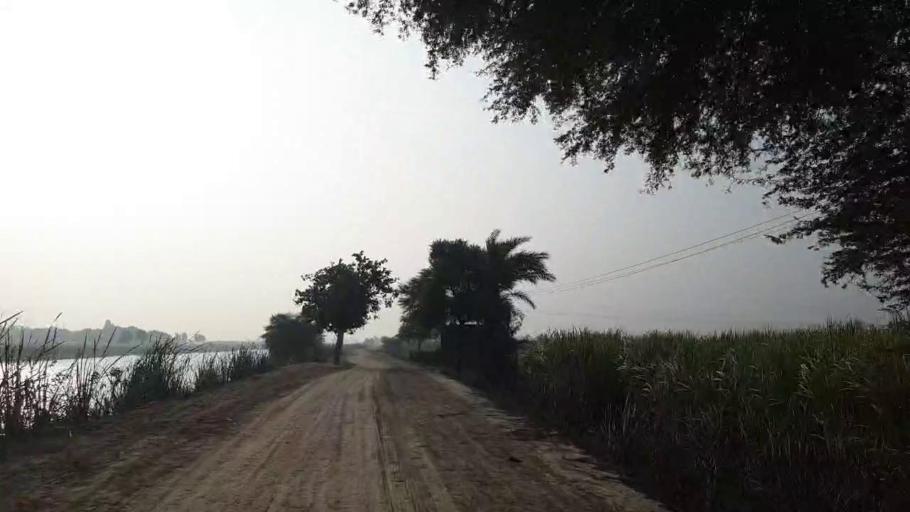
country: PK
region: Sindh
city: Tando Muhammad Khan
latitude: 25.1049
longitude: 68.5721
